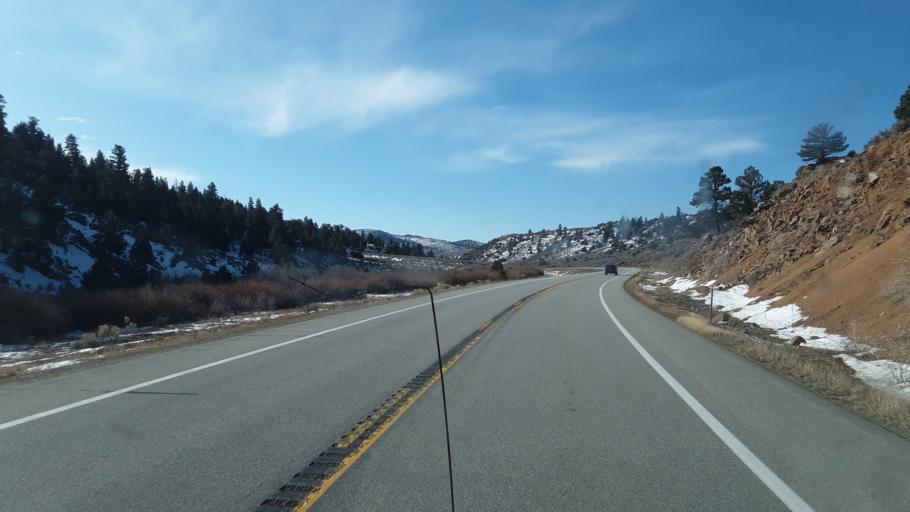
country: US
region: Colorado
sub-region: Costilla County
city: San Luis
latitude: 37.5325
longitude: -105.2942
